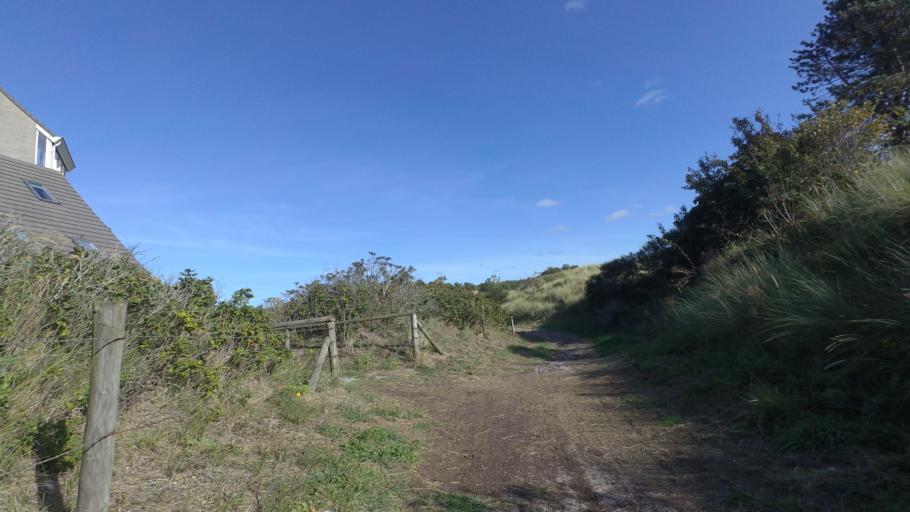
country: NL
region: Friesland
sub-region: Gemeente Ameland
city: Nes
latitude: 53.4554
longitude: 5.7734
